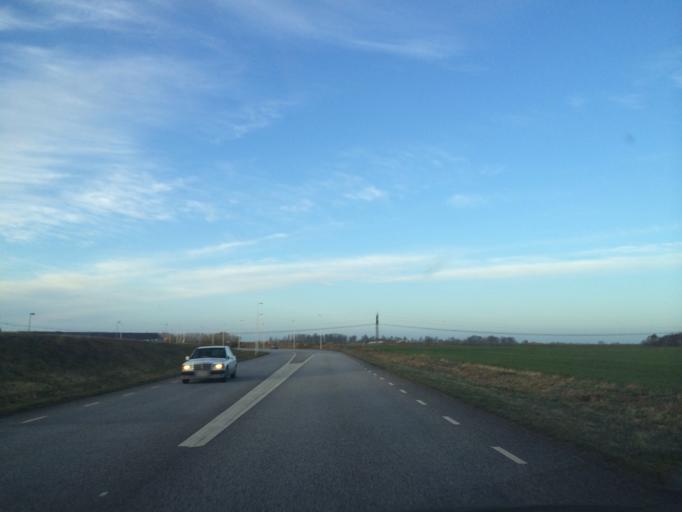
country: SE
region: Skane
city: Bjarred
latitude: 55.7370
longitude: 13.0399
